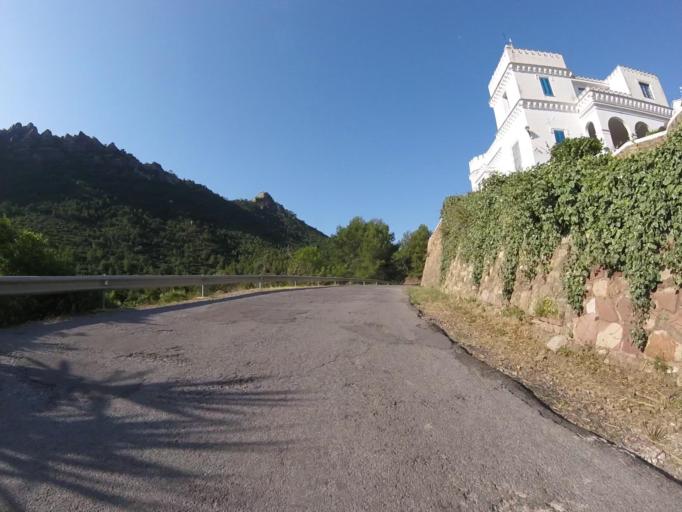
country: ES
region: Valencia
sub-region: Provincia de Castello
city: Benicassim
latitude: 40.0822
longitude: 0.0530
